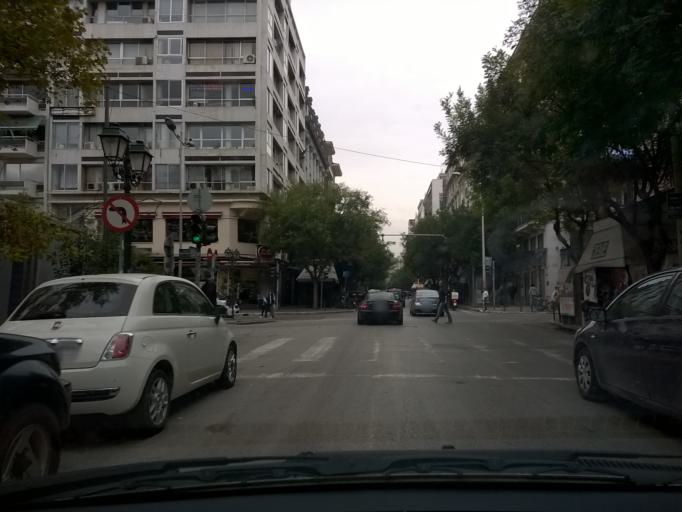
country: GR
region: Central Macedonia
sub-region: Nomos Thessalonikis
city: Thessaloniki
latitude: 40.6339
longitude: 22.9387
